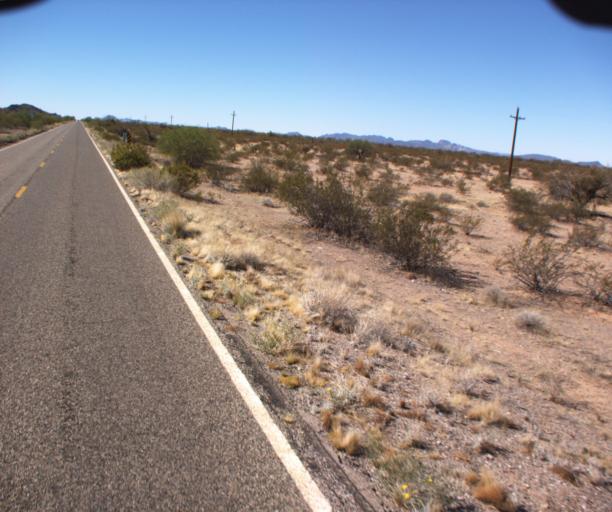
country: US
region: Arizona
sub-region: Pima County
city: Ajo
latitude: 32.2525
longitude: -112.7449
